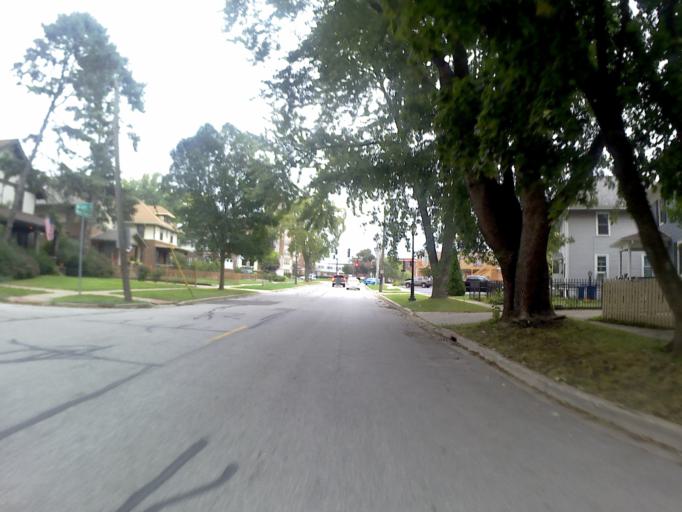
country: US
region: Illinois
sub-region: Kane County
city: Aurora
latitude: 41.7643
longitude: -88.3155
